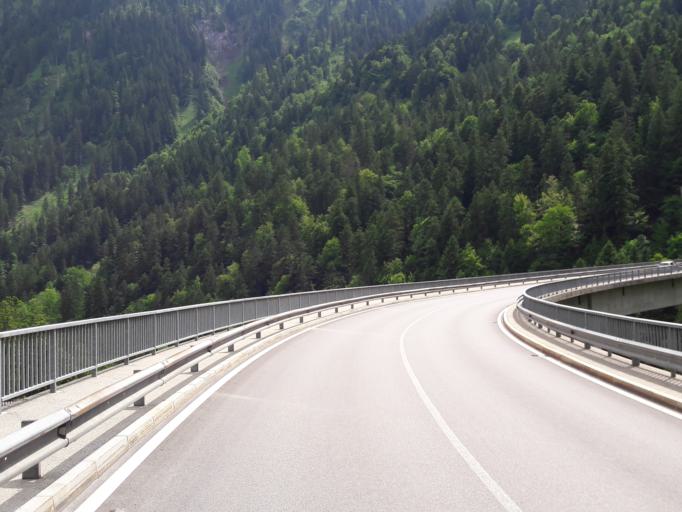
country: AT
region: Vorarlberg
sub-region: Politischer Bezirk Bludenz
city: Raggal
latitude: 47.2079
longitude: 9.8541
